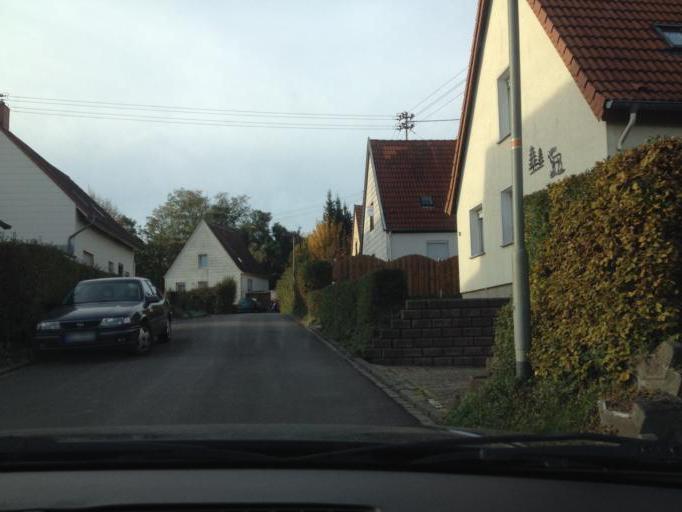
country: DE
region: Saarland
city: Ottweiler
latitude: 49.4121
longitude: 7.1521
